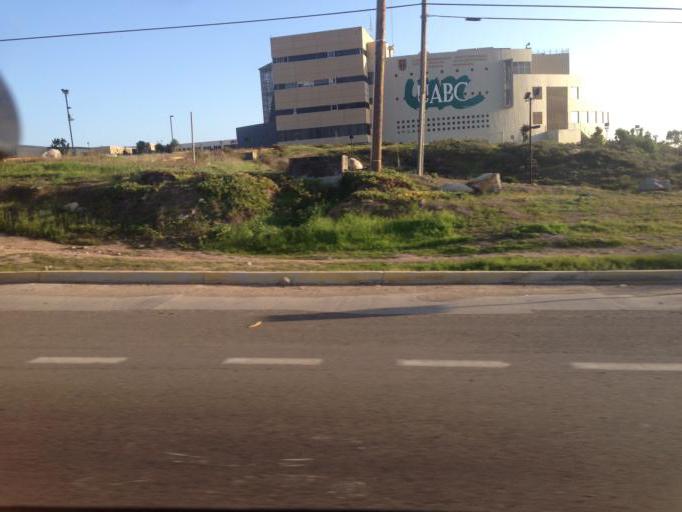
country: MX
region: Baja California
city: El Sauzal
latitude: 31.8666
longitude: -116.6666
